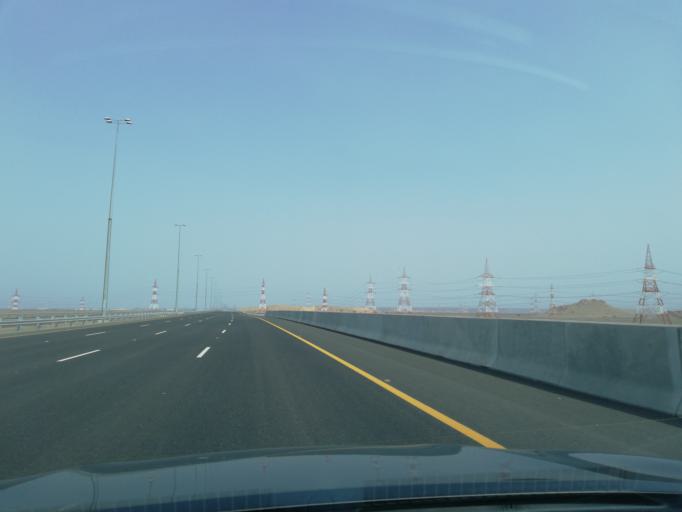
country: OM
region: Al Batinah
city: Al Sohar
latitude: 24.3302
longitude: 56.5598
